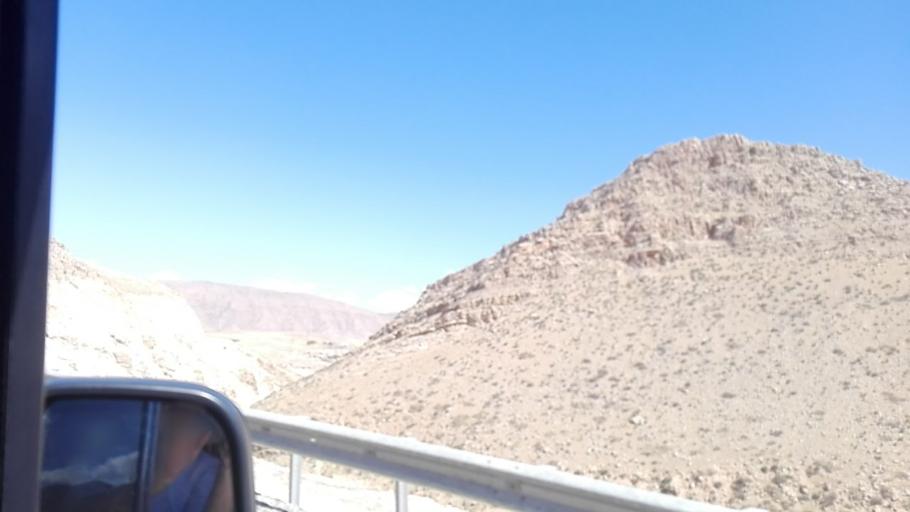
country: TR
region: Batman
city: Hasankeyf
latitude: 37.6958
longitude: 41.4587
